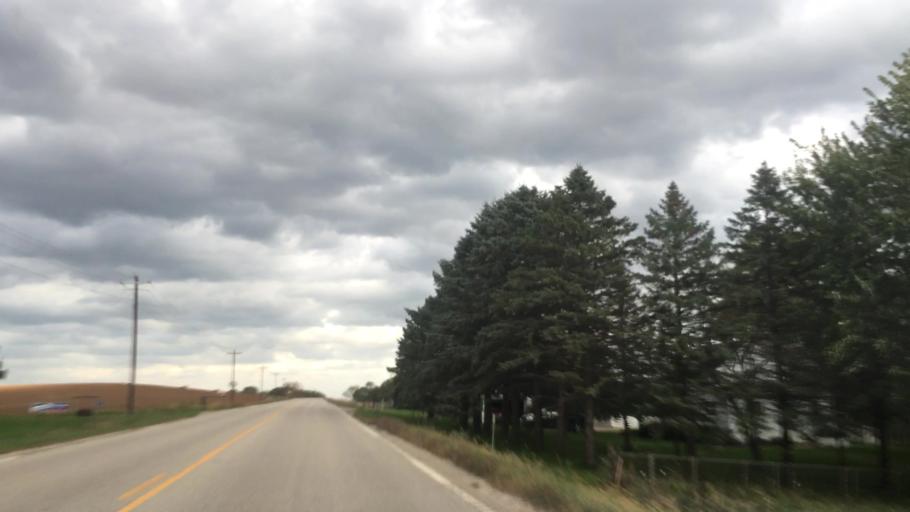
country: US
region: Minnesota
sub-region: Fillmore County
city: Preston
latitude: 43.7350
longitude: -92.0178
